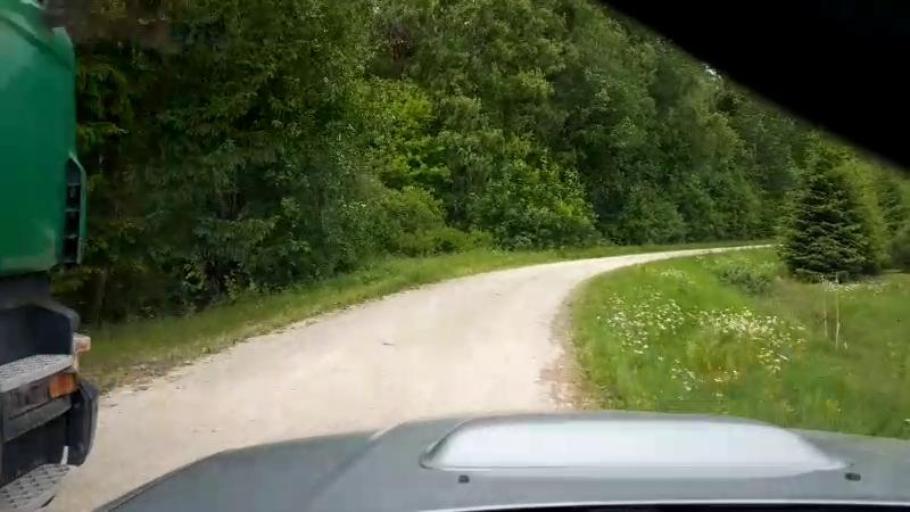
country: EE
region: Paernumaa
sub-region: Sindi linn
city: Sindi
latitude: 58.5198
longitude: 24.6190
